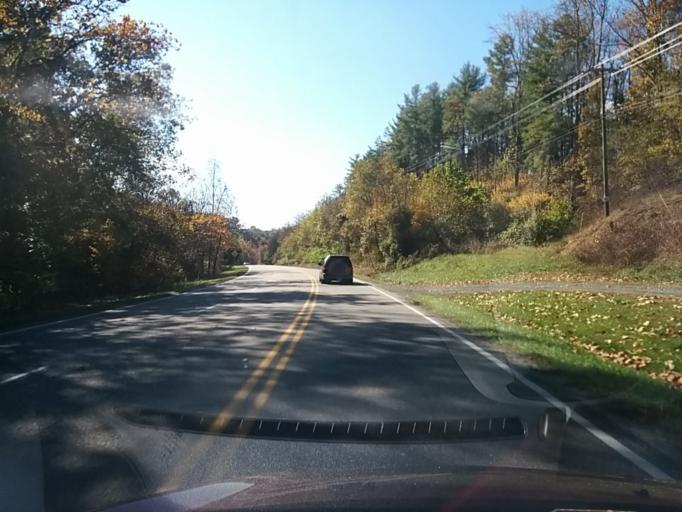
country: US
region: Virginia
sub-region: City of Lexington
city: Lexington
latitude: 37.7463
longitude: -79.4590
